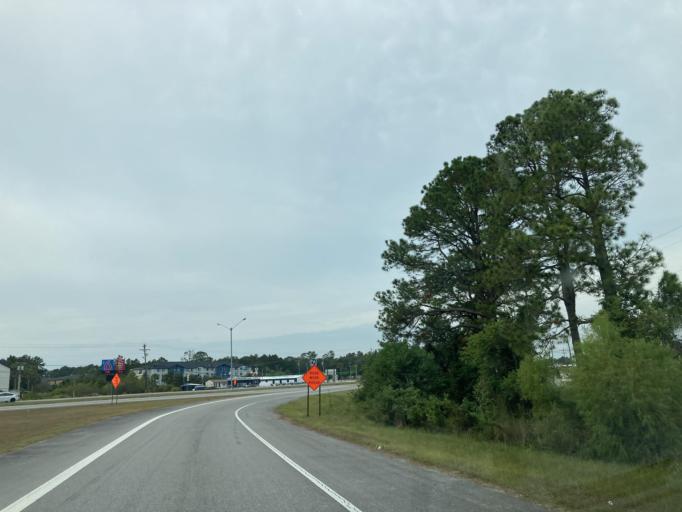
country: US
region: Mississippi
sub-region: Jackson County
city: Gulf Hills
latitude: 30.4555
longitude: -88.8424
